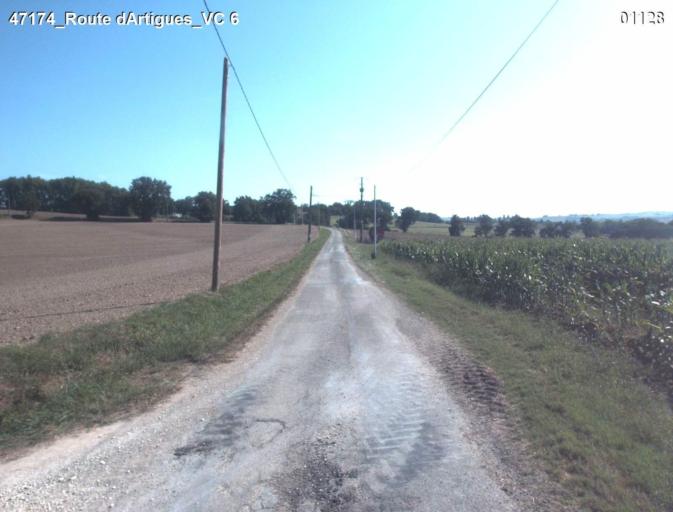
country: FR
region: Midi-Pyrenees
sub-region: Departement du Gers
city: Condom
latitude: 44.0178
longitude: 0.3319
